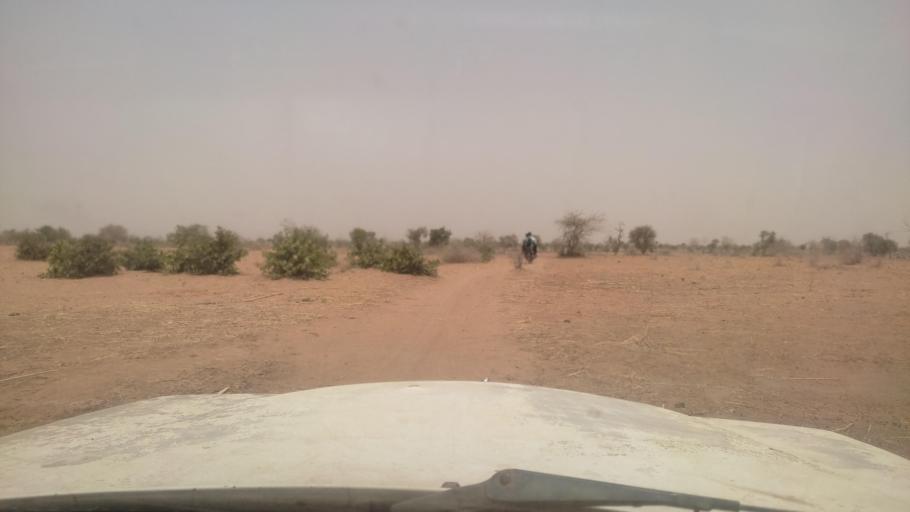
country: BF
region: Est
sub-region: Gnagna Province
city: Bogande
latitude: 13.0354
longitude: -0.0727
